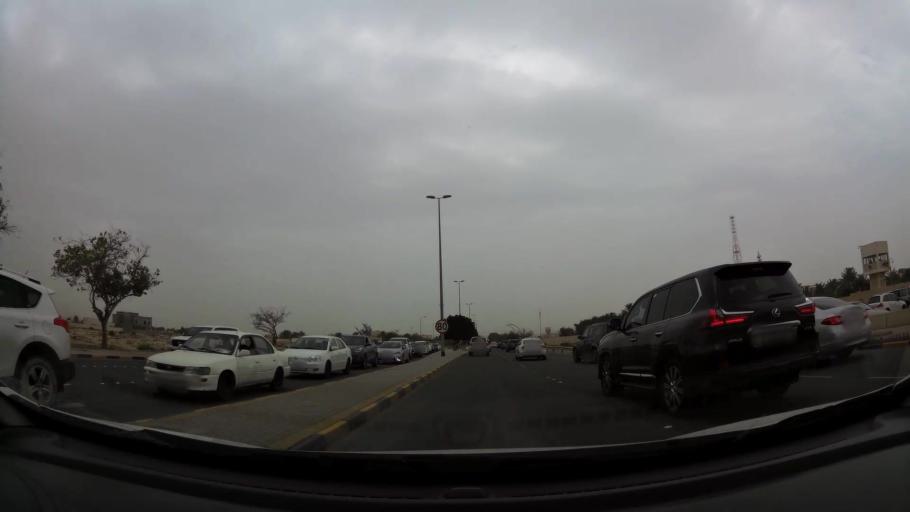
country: BH
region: Northern
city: Ar Rifa'
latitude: 26.1418
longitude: 50.5431
